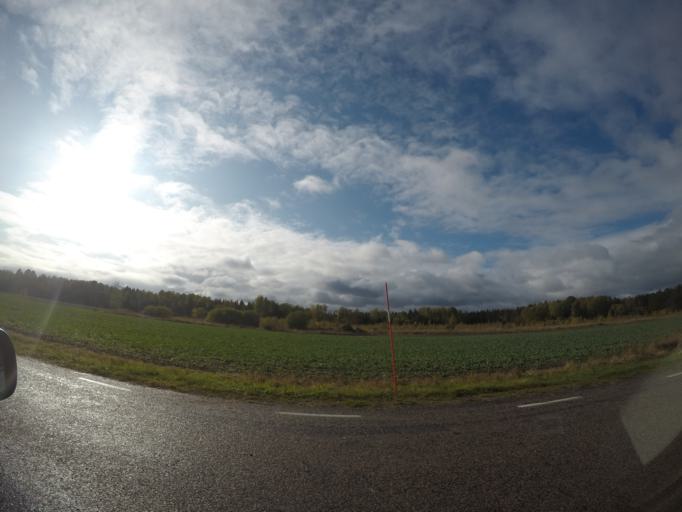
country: SE
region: Soedermanland
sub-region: Eskilstuna Kommun
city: Kvicksund
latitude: 59.3388
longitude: 16.2514
